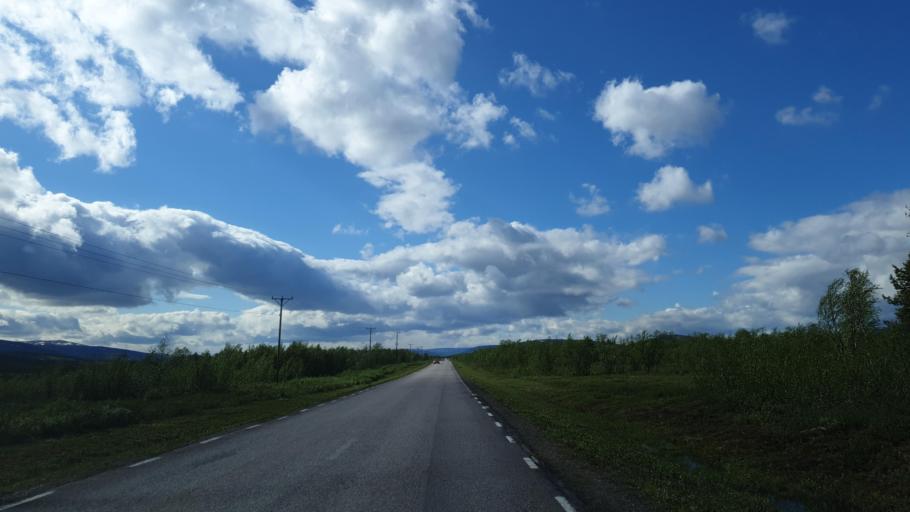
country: SE
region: Norrbotten
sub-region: Kiruna Kommun
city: Kiruna
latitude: 67.7588
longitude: 20.0162
